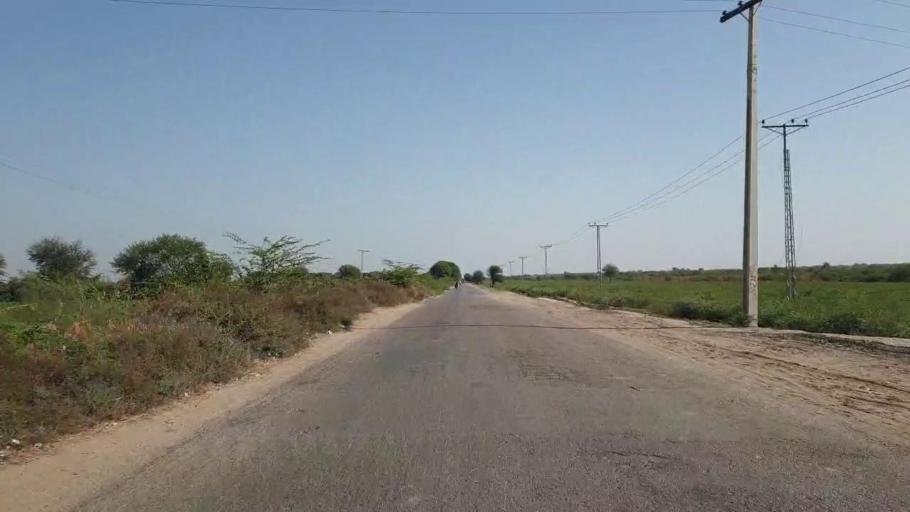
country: PK
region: Sindh
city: Umarkot
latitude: 25.4336
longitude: 69.7447
